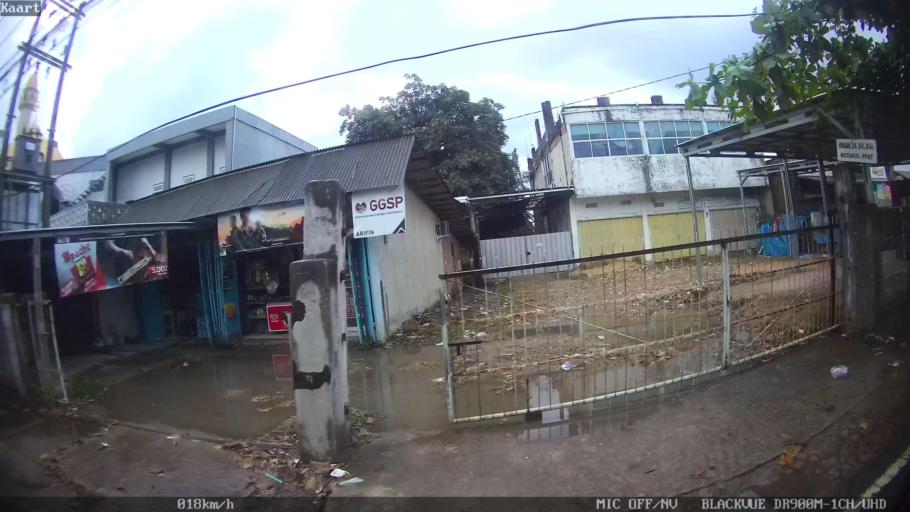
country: ID
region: Lampung
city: Kedaton
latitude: -5.3864
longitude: 105.2924
